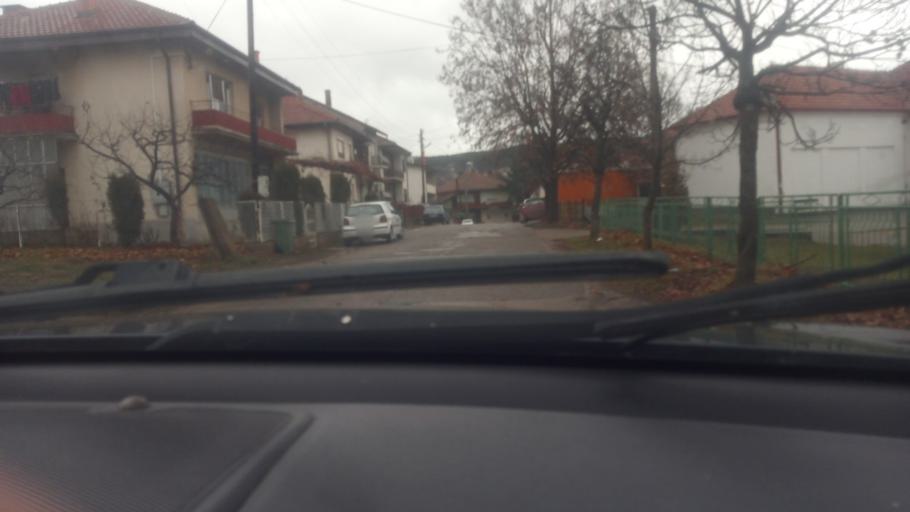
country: MK
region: Pehcevo
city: Pehcevo
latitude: 41.7627
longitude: 22.8843
